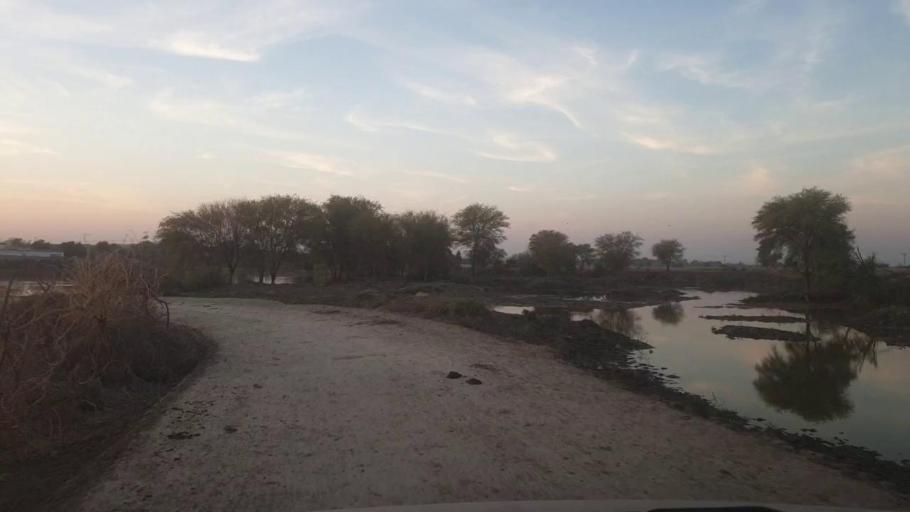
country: PK
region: Sindh
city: Hala
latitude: 25.7007
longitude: 68.3019
